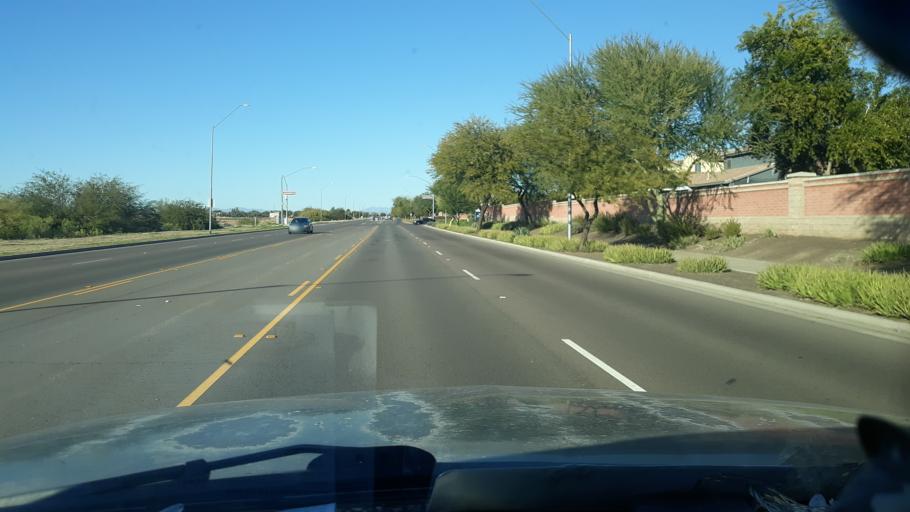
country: US
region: Arizona
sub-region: Maricopa County
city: Surprise
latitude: 33.6009
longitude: -112.3937
